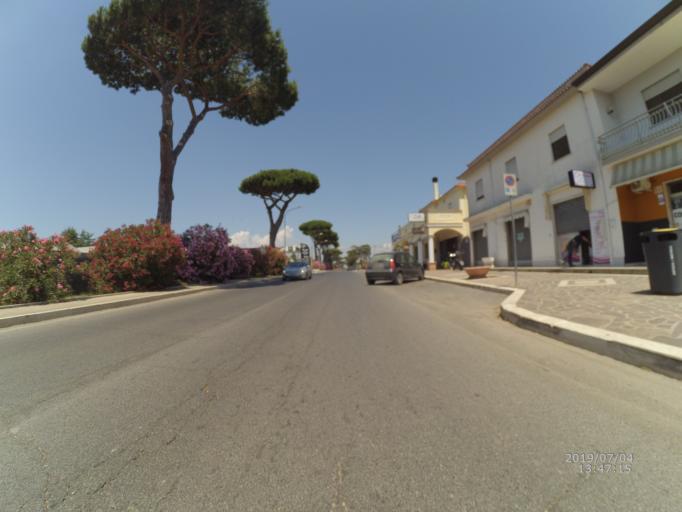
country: IT
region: Latium
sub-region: Provincia di Latina
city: San Felice Circeo
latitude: 41.2768
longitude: 13.1010
